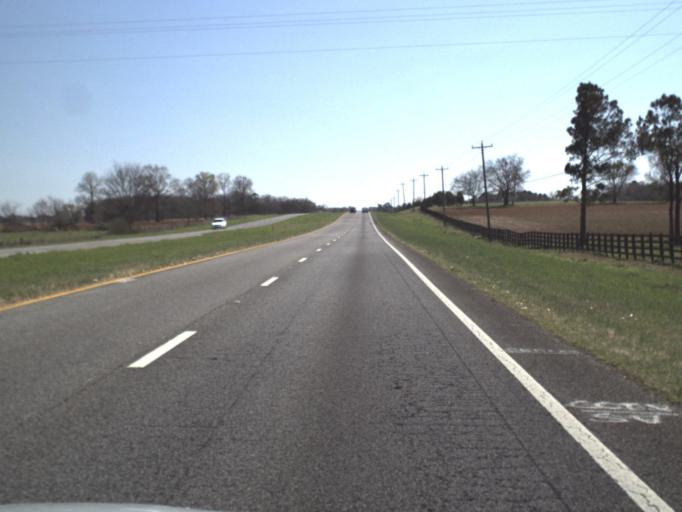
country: US
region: Florida
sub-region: Jackson County
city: Graceville
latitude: 30.9280
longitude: -85.3862
